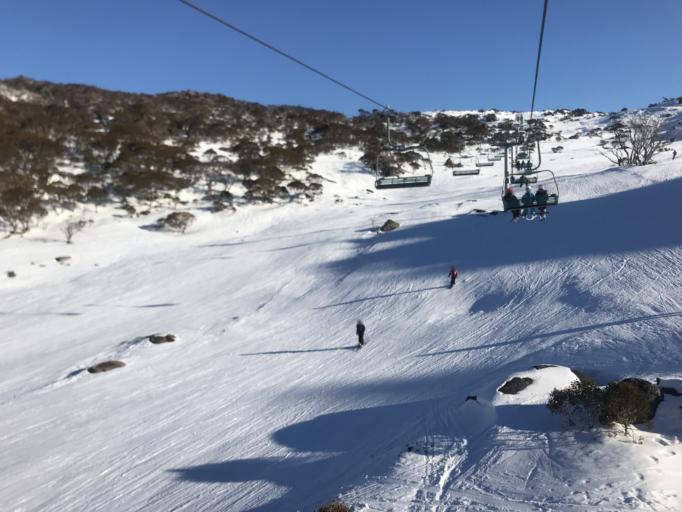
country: AU
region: New South Wales
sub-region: Snowy River
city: Jindabyne
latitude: -36.3891
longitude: 148.3973
